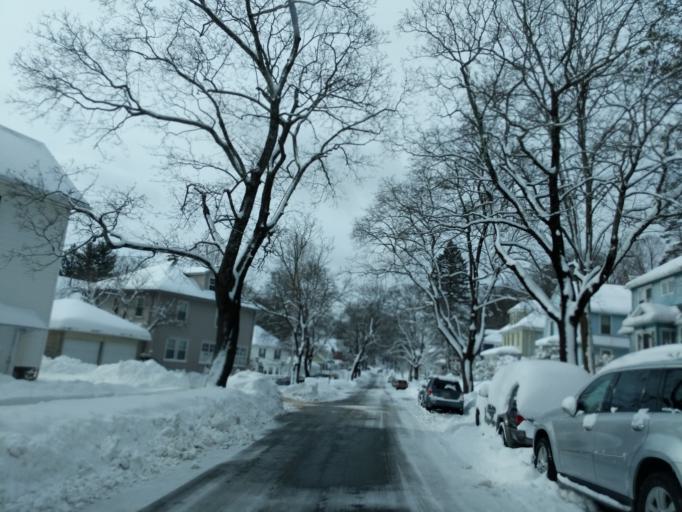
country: US
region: Massachusetts
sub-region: Worcester County
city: Worcester
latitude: 42.2696
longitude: -71.8302
